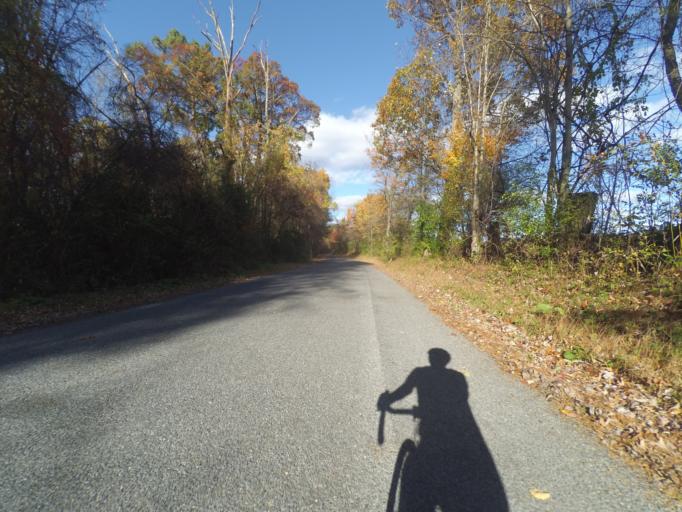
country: US
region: Pennsylvania
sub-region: Centre County
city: Houserville
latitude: 40.8718
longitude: -77.8144
